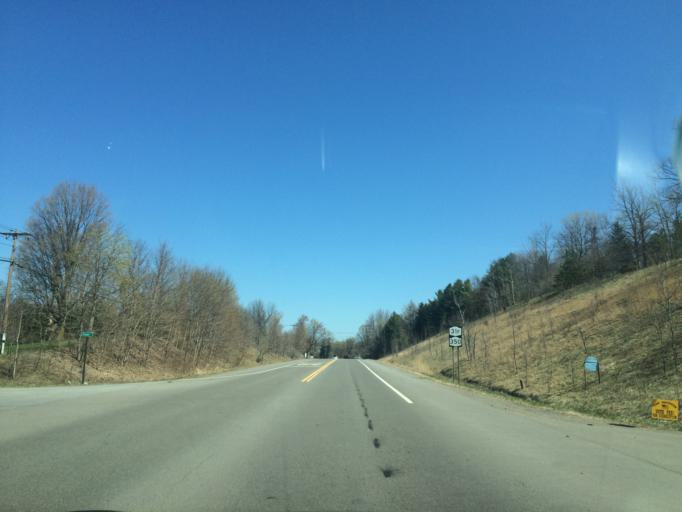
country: US
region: New York
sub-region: Wayne County
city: Macedon
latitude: 43.0765
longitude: -77.3014
